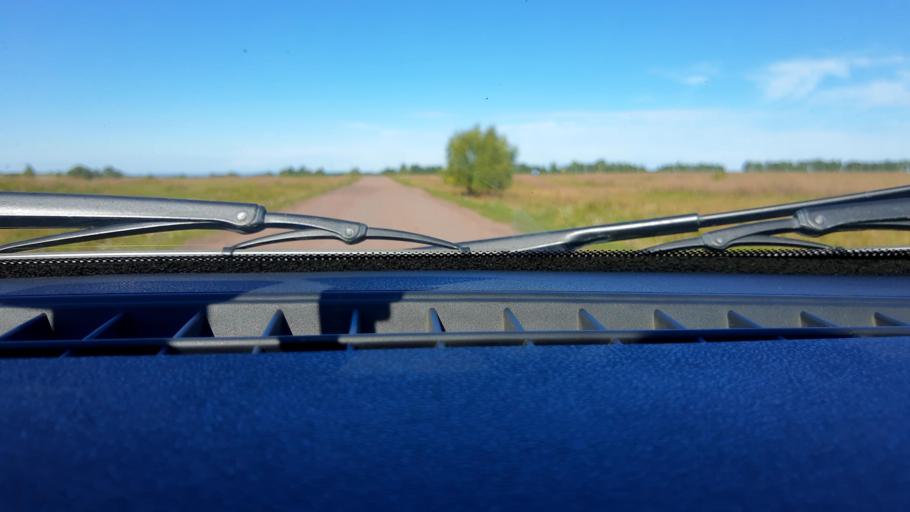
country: RU
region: Bashkortostan
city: Asanovo
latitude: 54.8223
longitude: 55.6237
